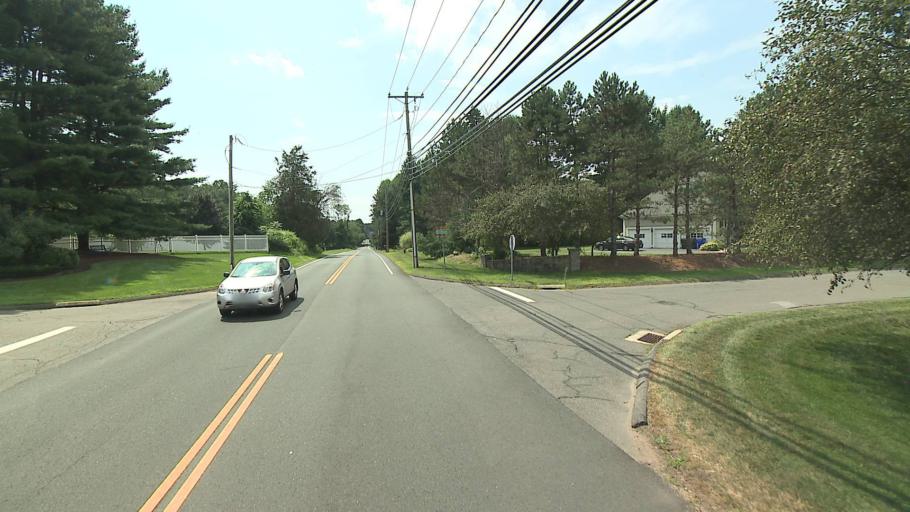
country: US
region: Connecticut
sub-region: Hartford County
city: Collinsville
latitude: 41.7732
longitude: -72.8906
